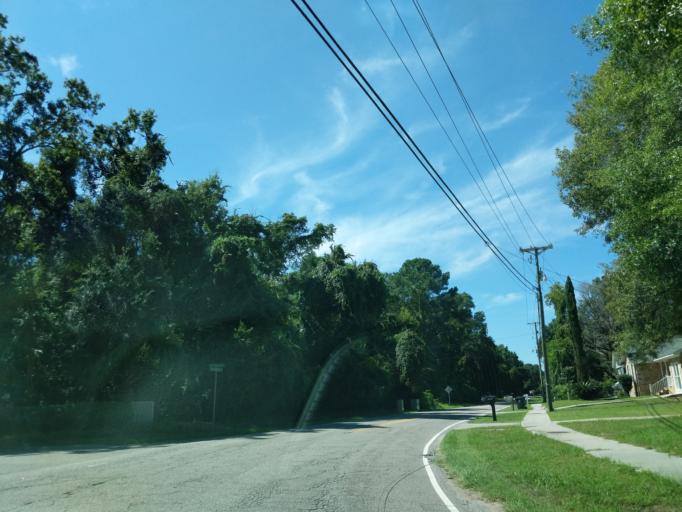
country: US
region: South Carolina
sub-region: Charleston County
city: Folly Beach
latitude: 32.7158
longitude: -79.9567
